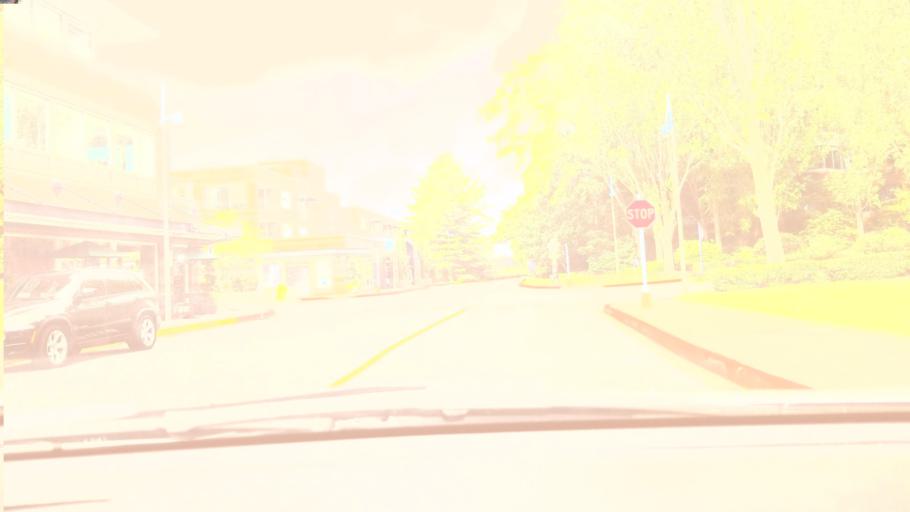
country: US
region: Washington
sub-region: King County
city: Yarrow Point
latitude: 47.6565
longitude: -122.2063
